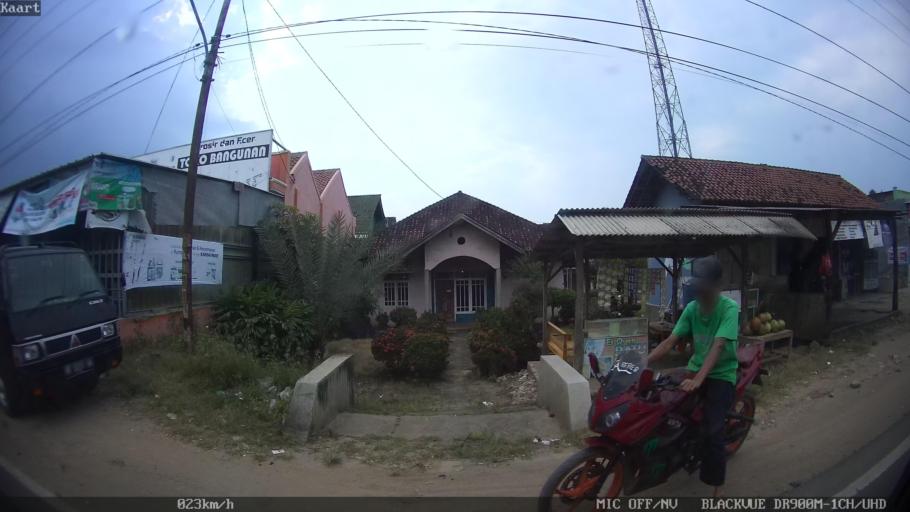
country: ID
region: Lampung
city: Gedongtataan
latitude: -5.3657
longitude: 105.1487
